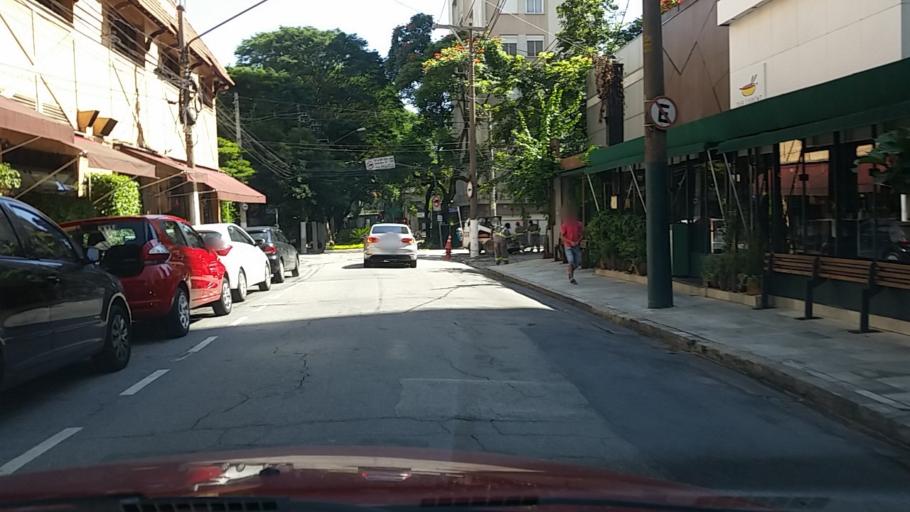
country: BR
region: Sao Paulo
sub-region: Sao Paulo
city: Sao Paulo
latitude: -23.5815
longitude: -46.6798
